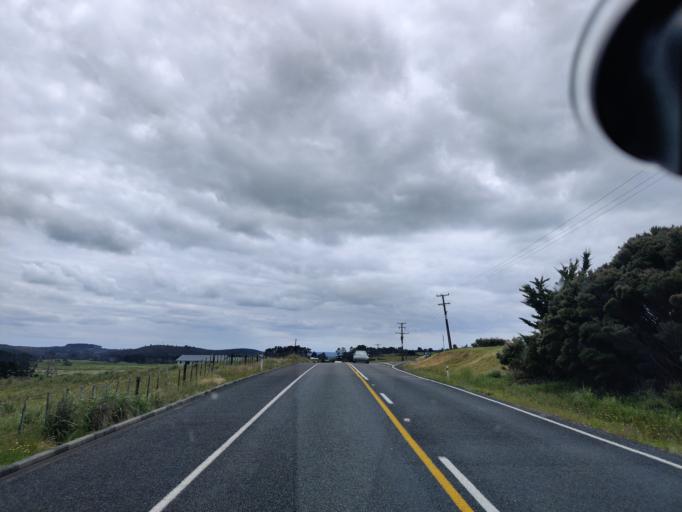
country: NZ
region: Northland
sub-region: Far North District
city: Kaitaia
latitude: -34.6460
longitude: 172.9702
